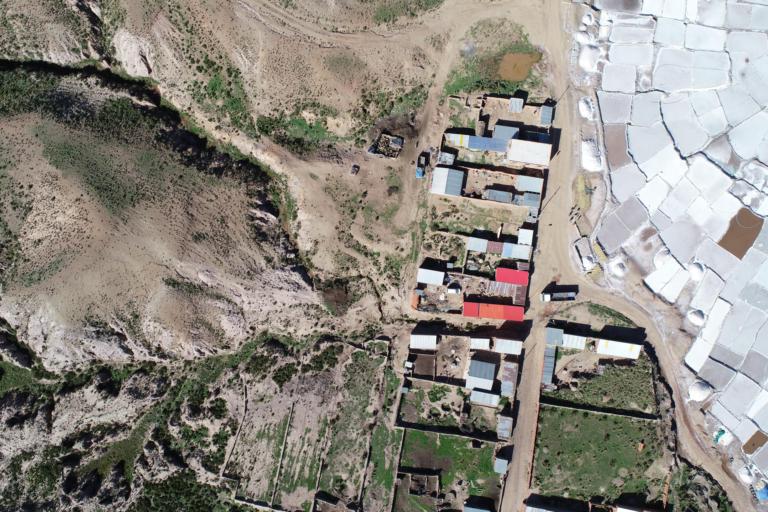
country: BO
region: La Paz
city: Patacamaya
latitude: -17.3015
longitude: -68.4832
